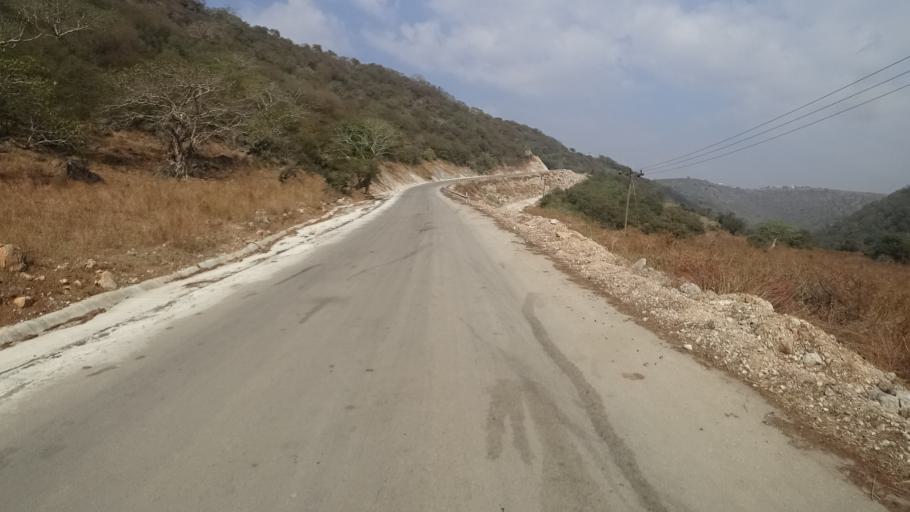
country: YE
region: Al Mahrah
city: Hawf
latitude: 16.7214
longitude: 53.2702
